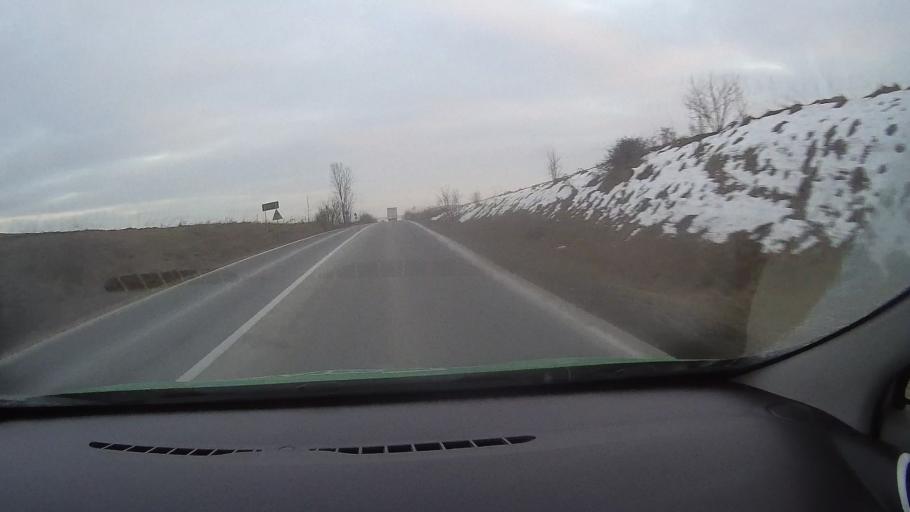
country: RO
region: Harghita
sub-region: Comuna Lupeni
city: Lupeni
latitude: 46.3590
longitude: 25.2497
